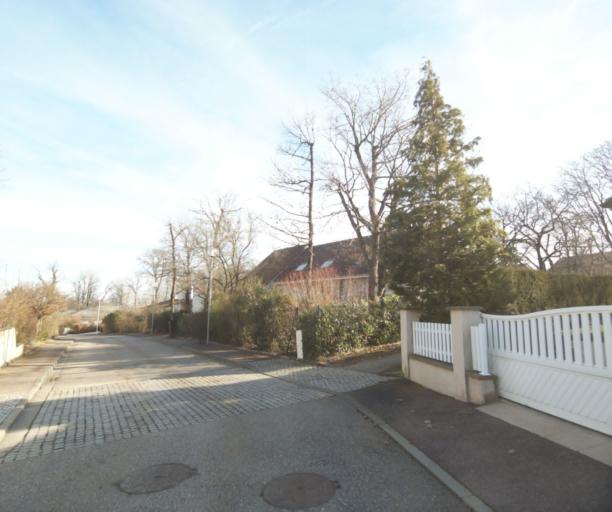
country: FR
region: Lorraine
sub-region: Departement de Meurthe-et-Moselle
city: Villers-les-Nancy
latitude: 48.6478
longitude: 6.1559
